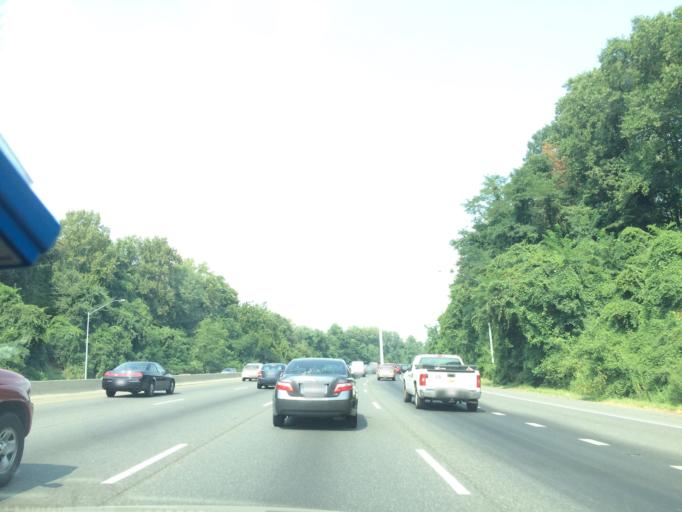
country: US
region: Maryland
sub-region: Montgomery County
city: Cabin John
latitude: 38.9778
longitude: -77.1774
